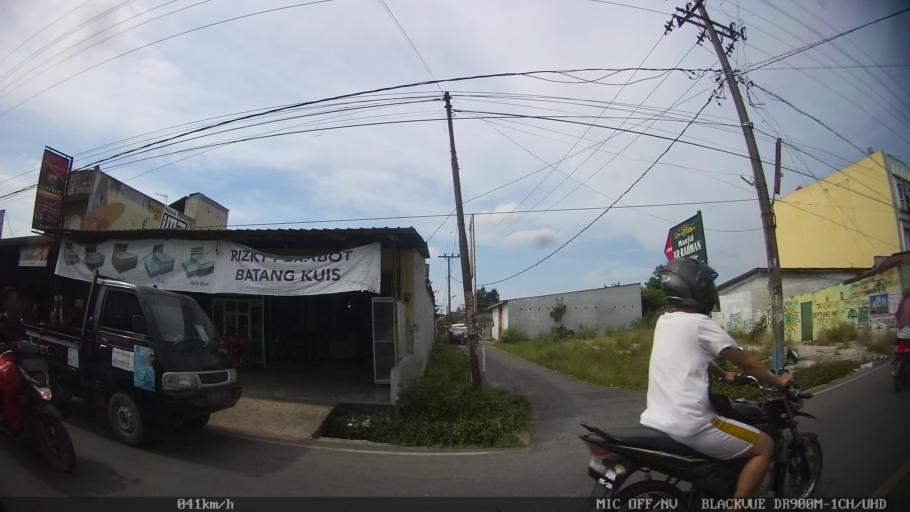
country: ID
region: North Sumatra
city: Percut
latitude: 3.6073
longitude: 98.7647
